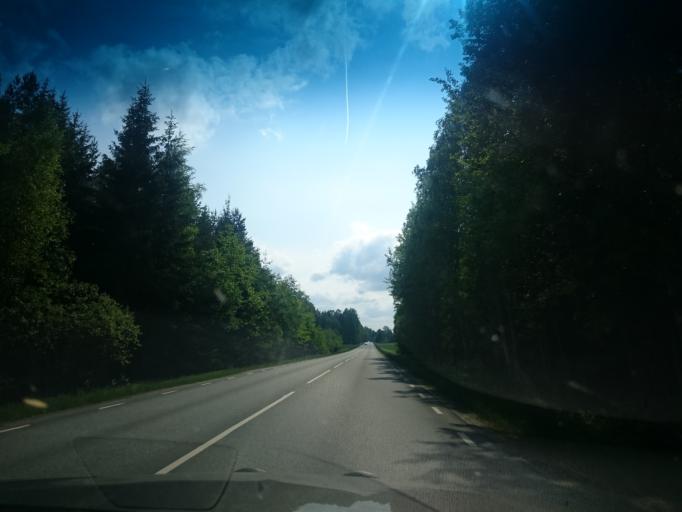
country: SE
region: Joenkoeping
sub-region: Vetlanda Kommun
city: Landsbro
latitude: 57.3920
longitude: 14.9822
